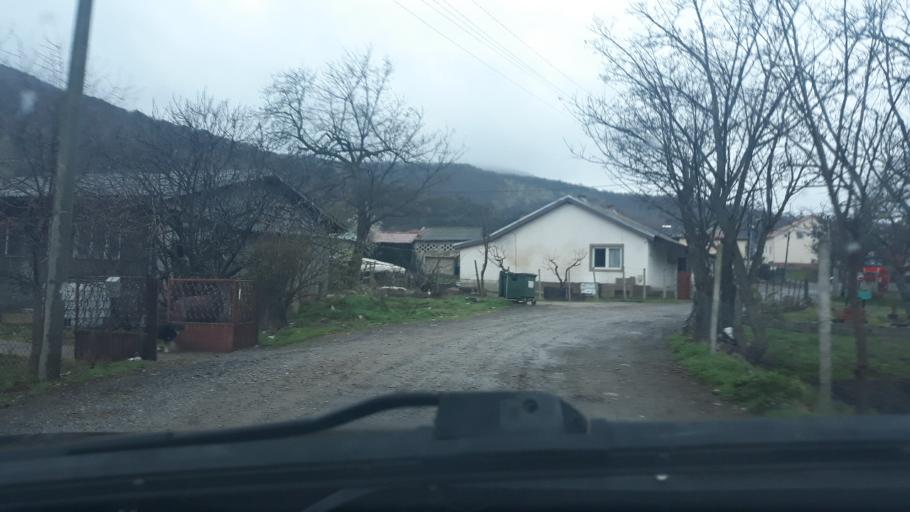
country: MK
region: Dojran
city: Star Dojran
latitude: 41.2367
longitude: 22.6560
